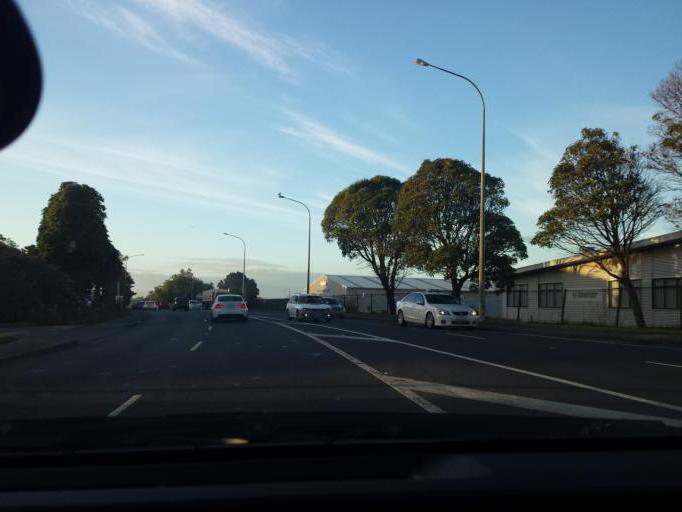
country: NZ
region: Auckland
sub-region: Auckland
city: Tamaki
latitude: -36.9143
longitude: 174.8209
